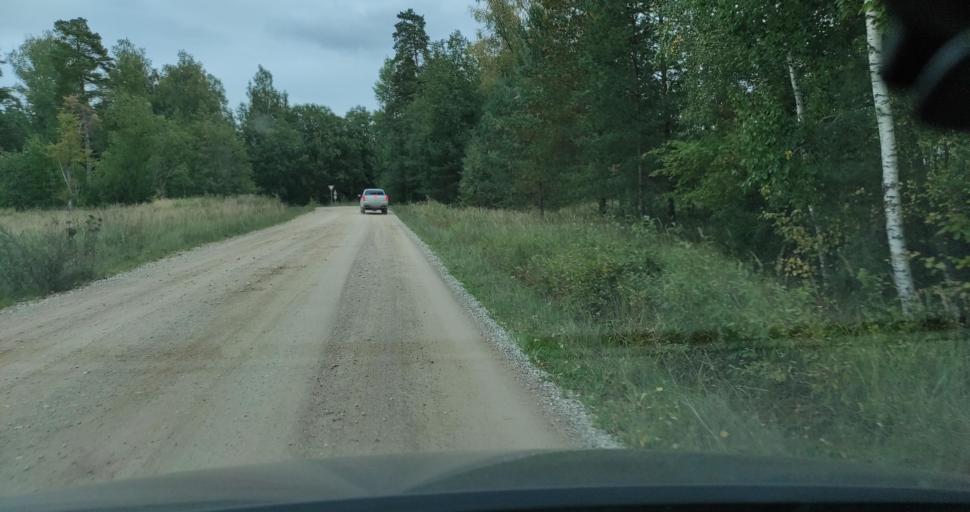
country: LV
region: Talsu Rajons
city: Stende
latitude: 57.0842
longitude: 22.2609
